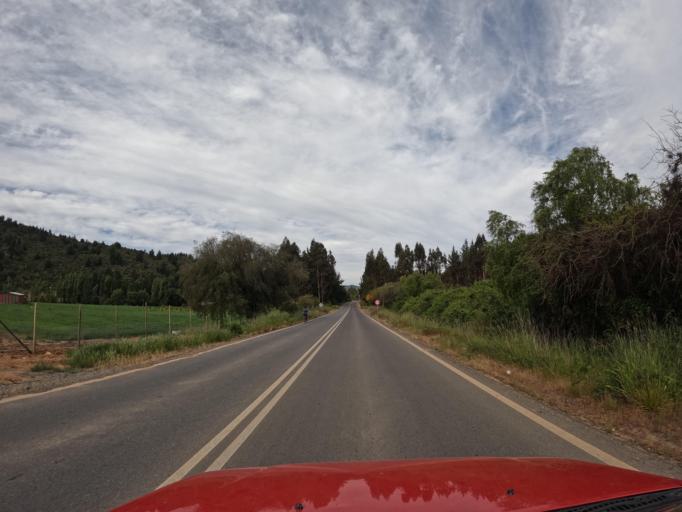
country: CL
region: Maule
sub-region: Provincia de Talca
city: Talca
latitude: -35.3227
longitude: -71.9467
